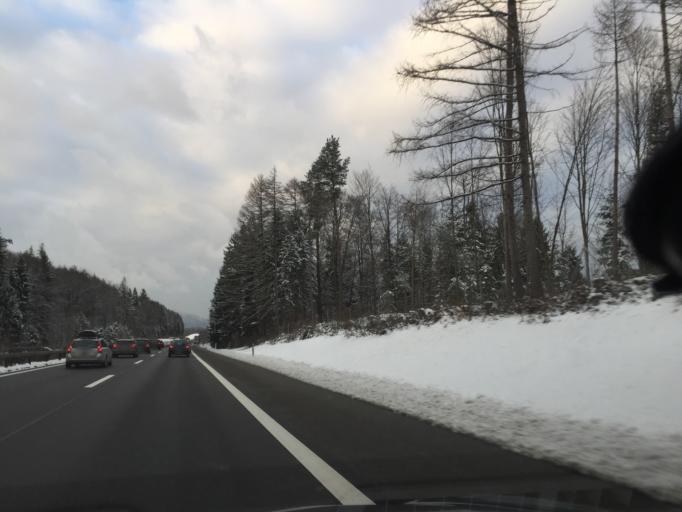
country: CH
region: Zurich
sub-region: Bezirk Horgen
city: Oberrieden / Berg
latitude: 47.2772
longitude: 8.5645
